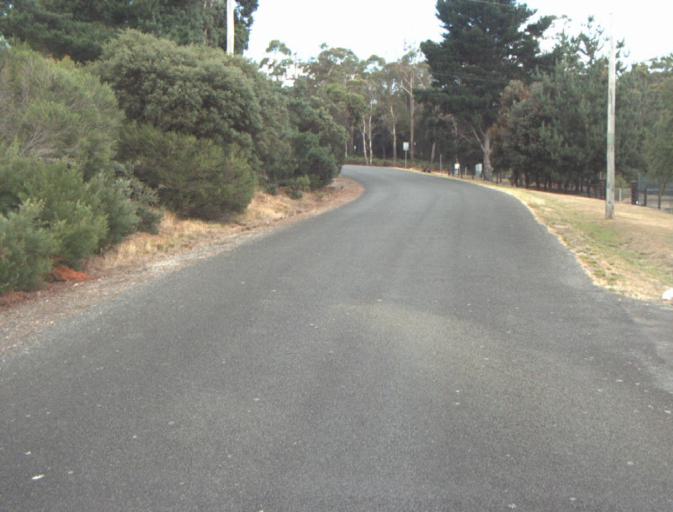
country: AU
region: Tasmania
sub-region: Launceston
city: Mayfield
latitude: -41.2815
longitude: 147.0197
